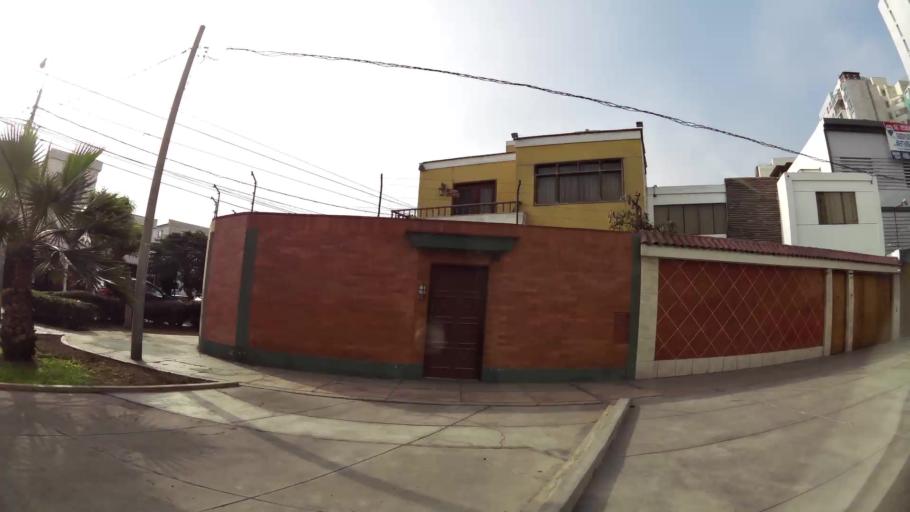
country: PE
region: Lima
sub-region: Lima
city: San Isidro
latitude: -12.0920
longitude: -77.0599
